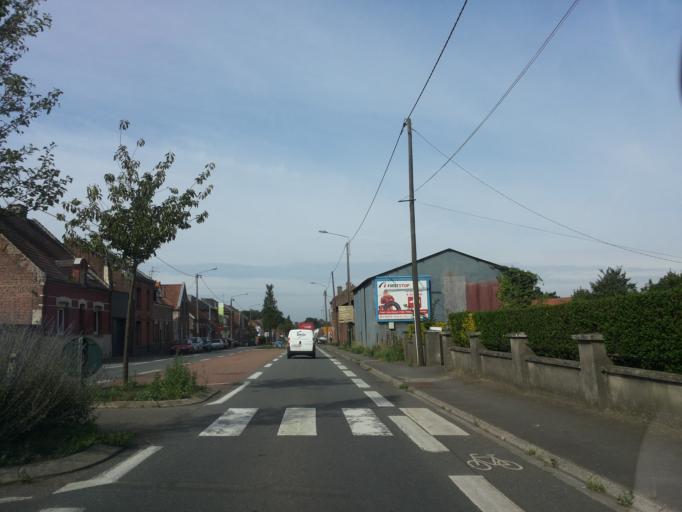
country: FR
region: Nord-Pas-de-Calais
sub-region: Departement du Pas-de-Calais
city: Tilloy-les-Mofflaines
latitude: 50.2783
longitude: 2.8214
